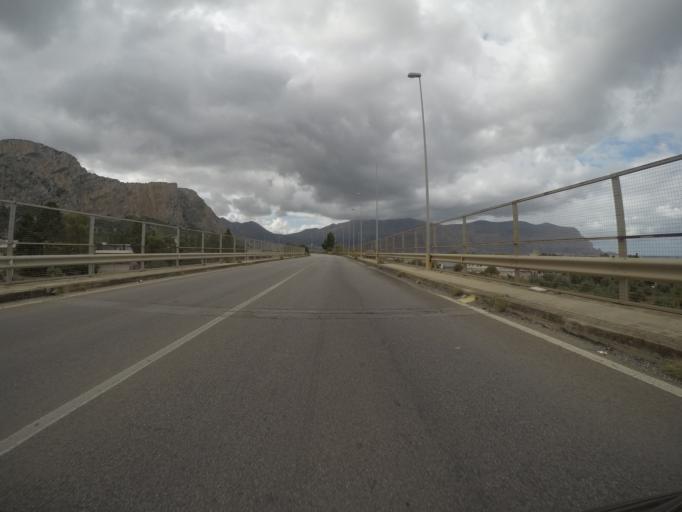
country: IT
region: Sicily
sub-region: Palermo
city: Capaci
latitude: 38.1652
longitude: 13.2207
